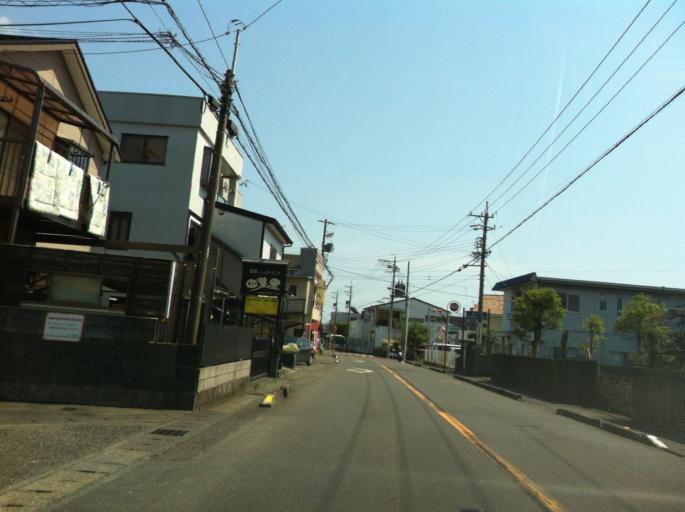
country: JP
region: Shizuoka
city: Shizuoka-shi
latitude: 35.0154
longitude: 138.4230
